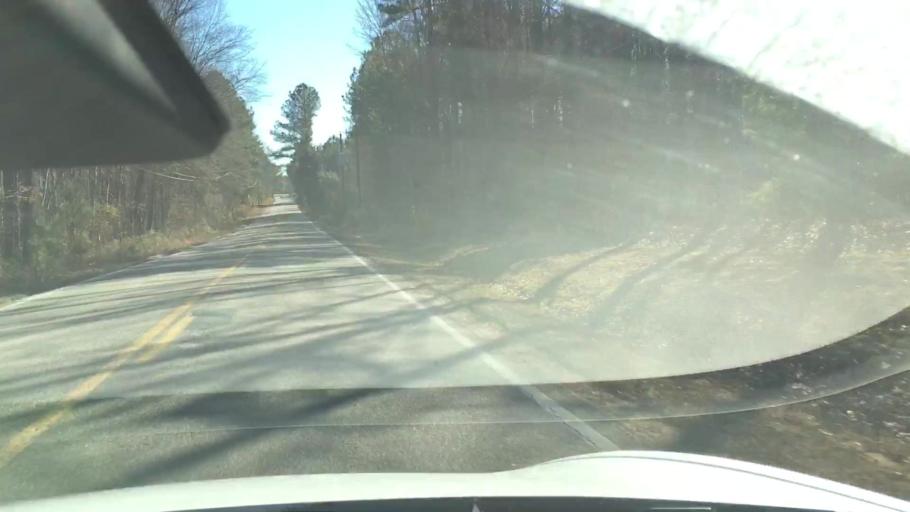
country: US
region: Virginia
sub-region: Henrico County
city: Short Pump
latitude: 37.5722
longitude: -77.7173
